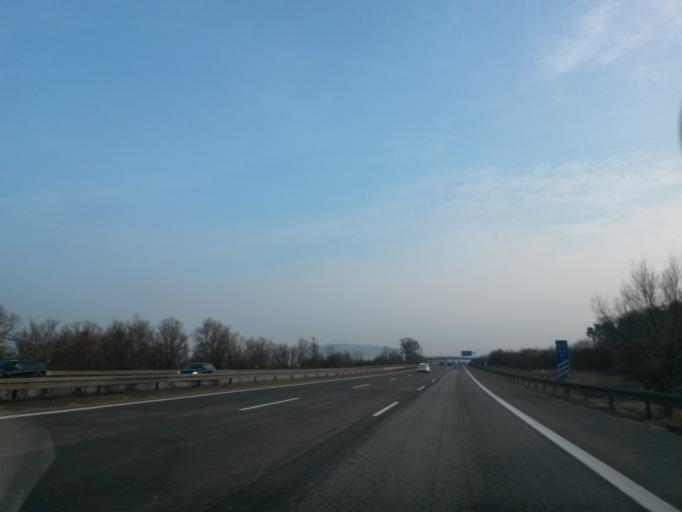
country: DE
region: Bavaria
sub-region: Regierungsbezirk Mittelfranken
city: Hilpoltstein
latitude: 49.1726
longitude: 11.2615
